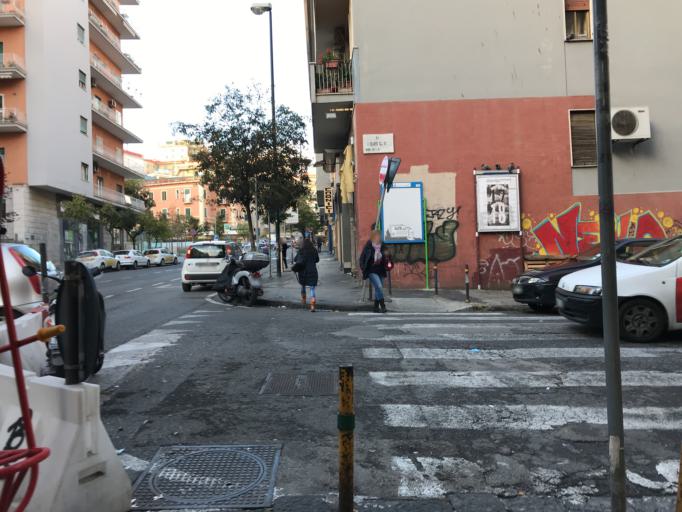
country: IT
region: Campania
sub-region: Provincia di Napoli
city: Napoli
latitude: 40.8525
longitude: 14.2305
